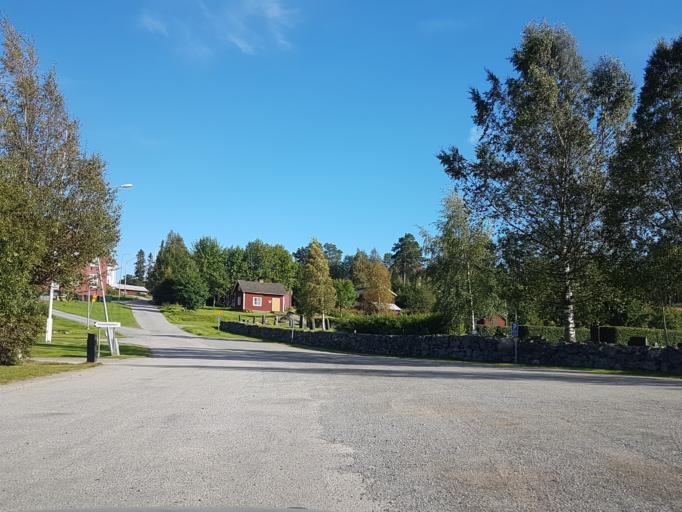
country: SE
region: Vaesterbotten
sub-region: Robertsfors Kommun
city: Robertsfors
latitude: 64.0630
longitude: 20.8624
